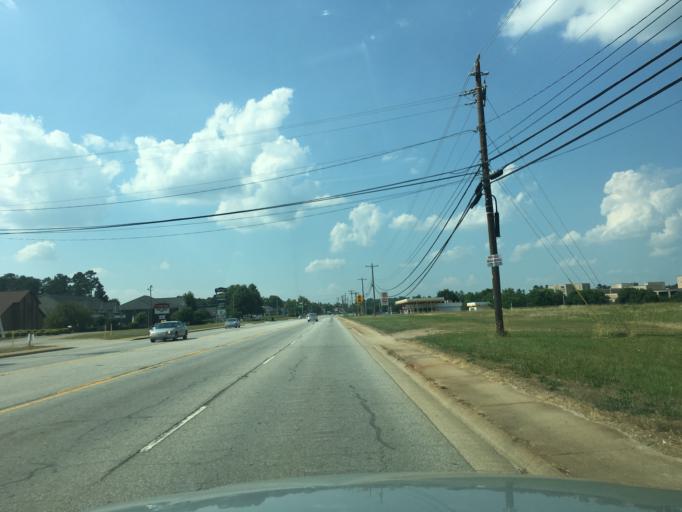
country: US
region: South Carolina
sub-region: Anderson County
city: Anderson
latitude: 34.5412
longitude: -82.6305
